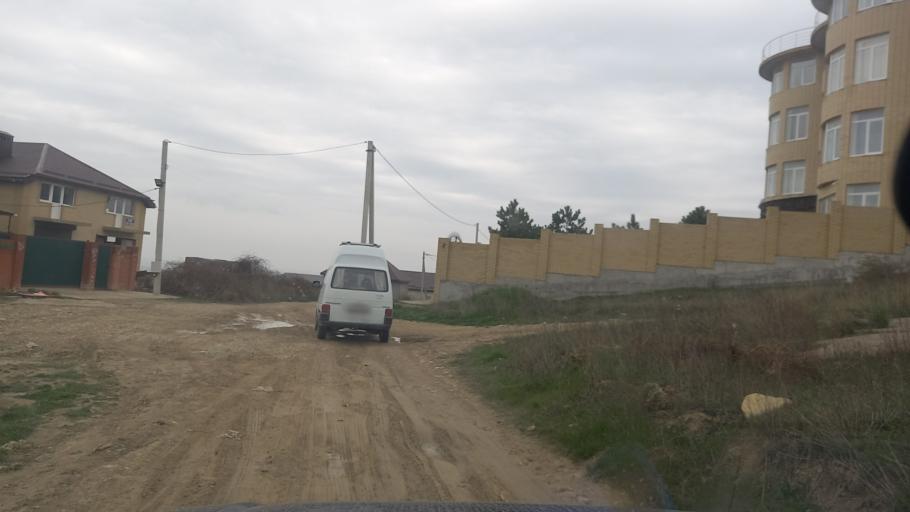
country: RU
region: Krasnodarskiy
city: Anapa
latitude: 44.8557
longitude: 37.3410
